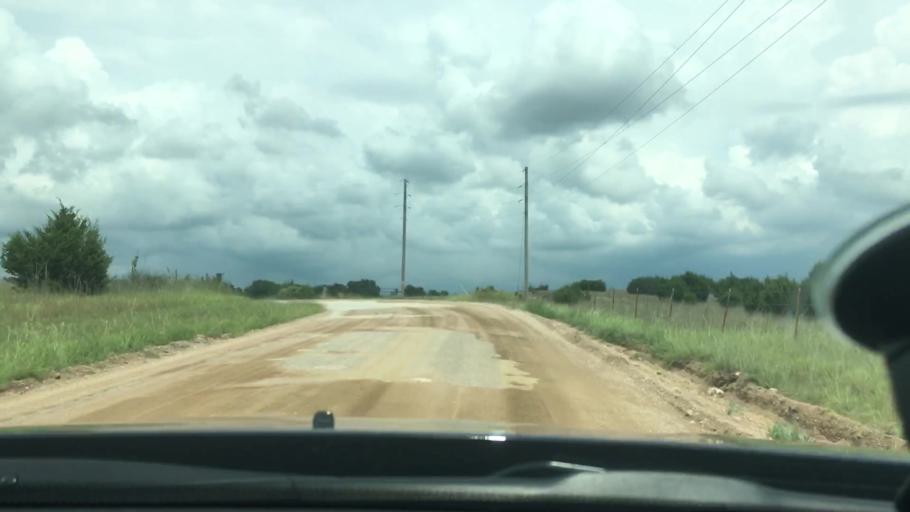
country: US
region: Oklahoma
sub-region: Carter County
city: Dickson
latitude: 34.2519
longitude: -96.9289
